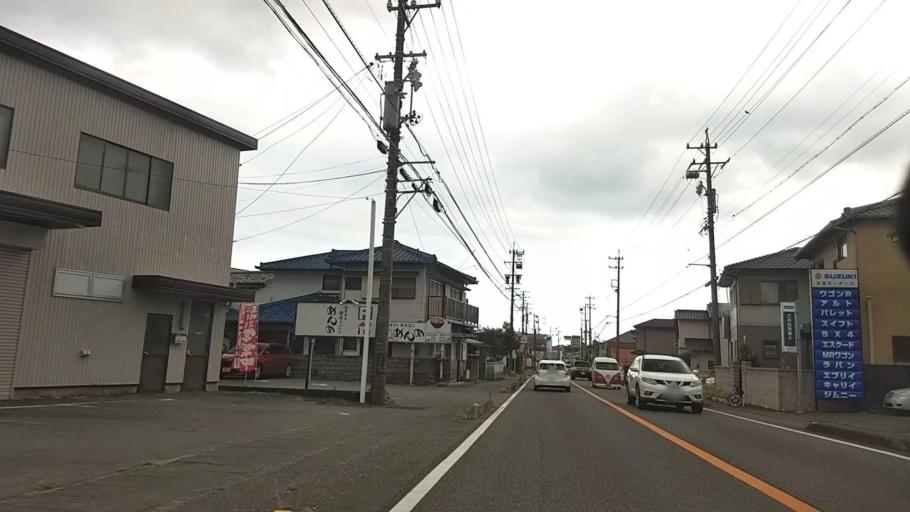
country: JP
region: Shizuoka
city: Shizuoka-shi
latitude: 35.0685
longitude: 138.5224
